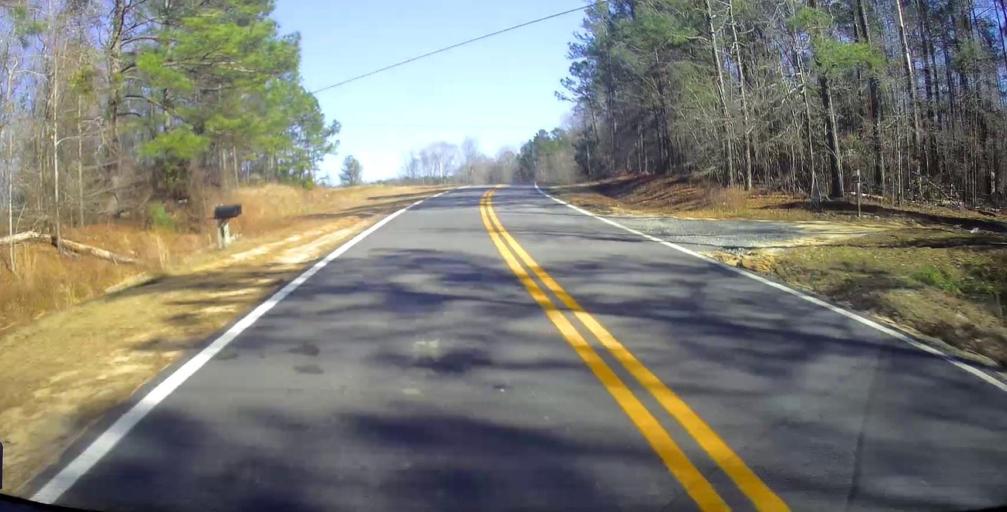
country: US
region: Georgia
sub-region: Peach County
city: Fort Valley
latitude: 32.6421
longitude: -83.9167
